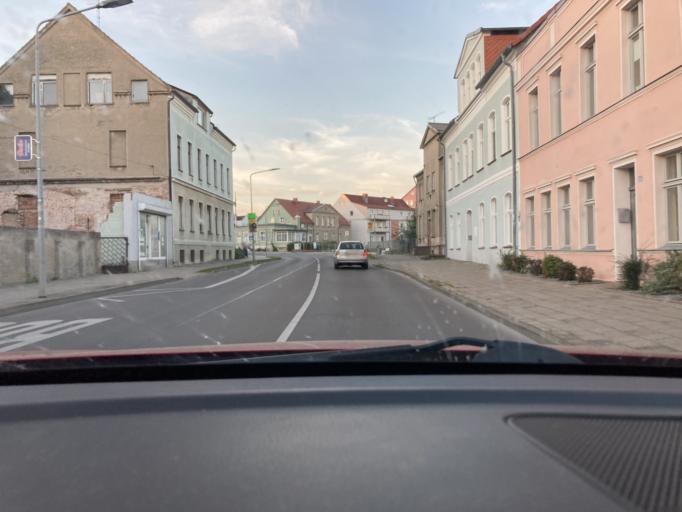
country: DE
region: Mecklenburg-Vorpommern
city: Anklam
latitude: 53.8541
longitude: 13.6929
